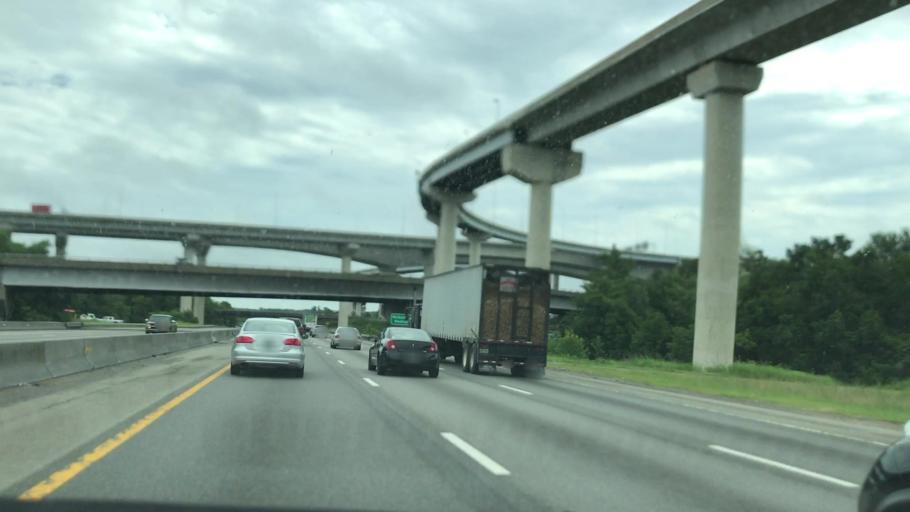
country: US
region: Virginia
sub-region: Chesterfield County
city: Bensley
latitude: 37.4401
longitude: -77.4279
